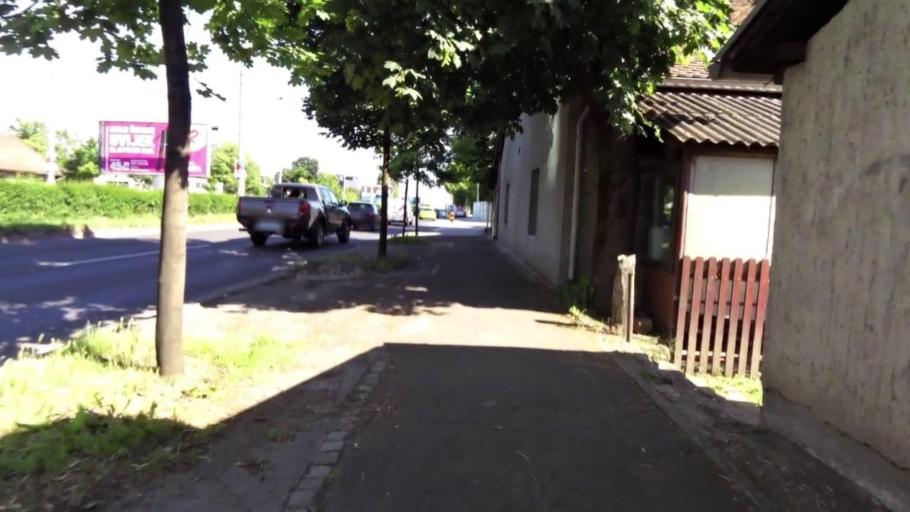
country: HR
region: Grad Zagreb
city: Novi Zagreb
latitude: 45.8010
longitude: 16.0122
